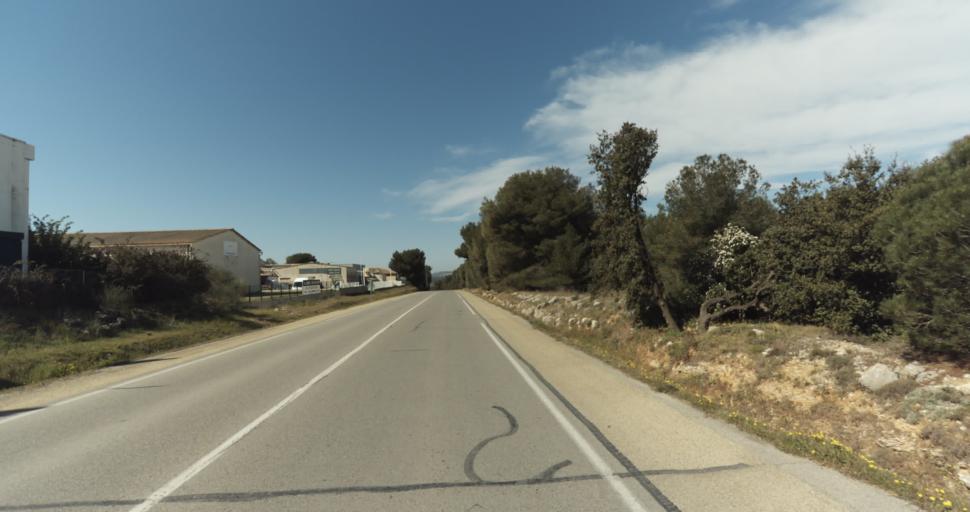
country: FR
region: Provence-Alpes-Cote d'Azur
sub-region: Departement des Bouches-du-Rhone
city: Lambesc
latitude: 43.6492
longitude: 5.2583
